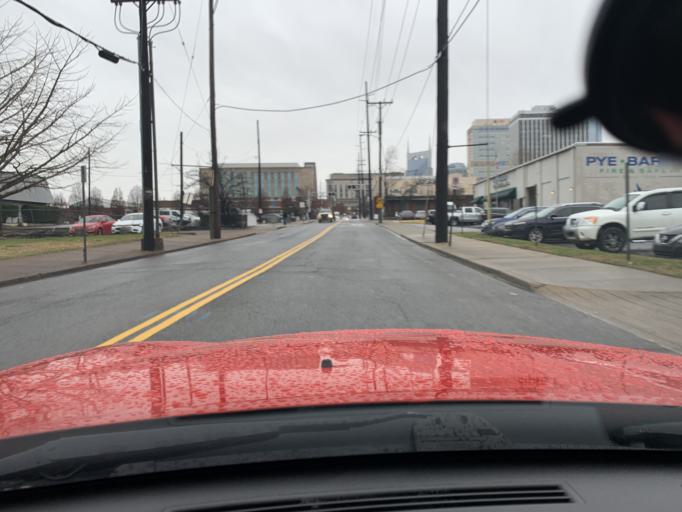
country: US
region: Tennessee
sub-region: Davidson County
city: Nashville
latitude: 36.1715
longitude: -86.7812
